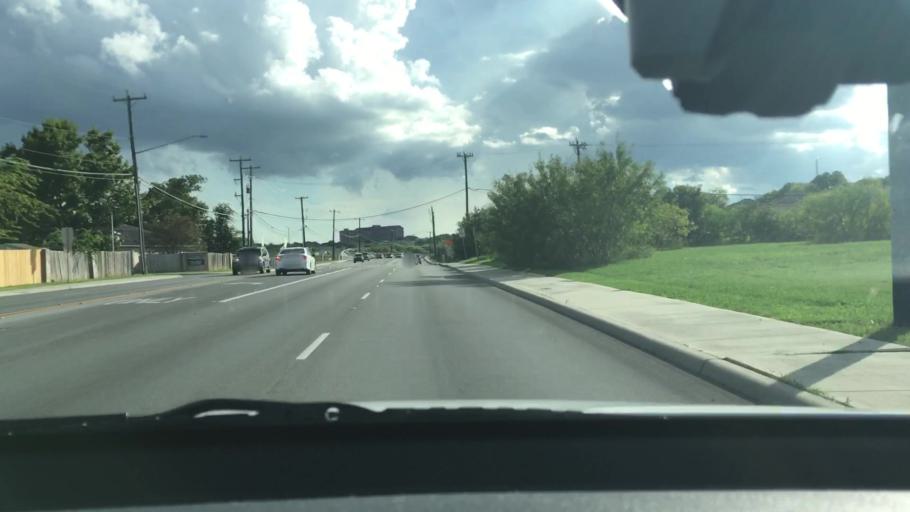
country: US
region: Texas
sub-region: Bexar County
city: Converse
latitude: 29.5300
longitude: -98.3369
